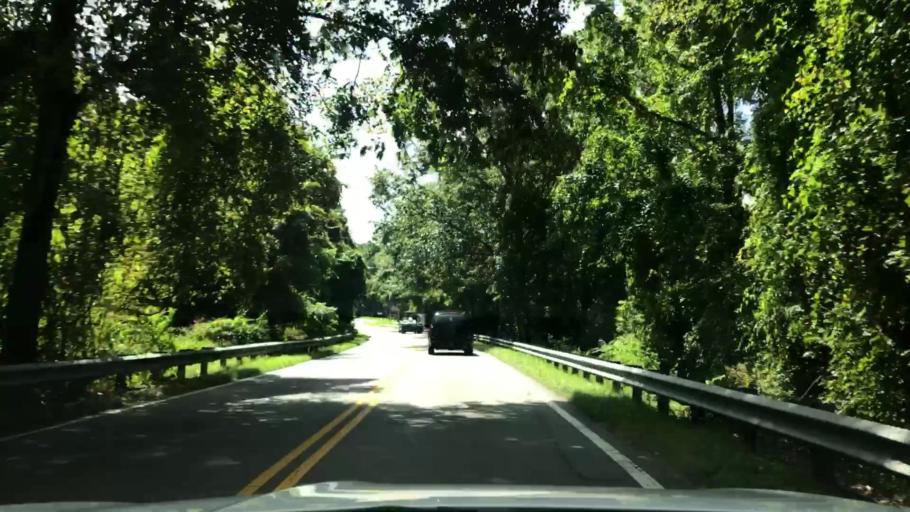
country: US
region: South Carolina
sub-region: Charleston County
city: Shell Point
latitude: 32.8412
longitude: -80.0554
